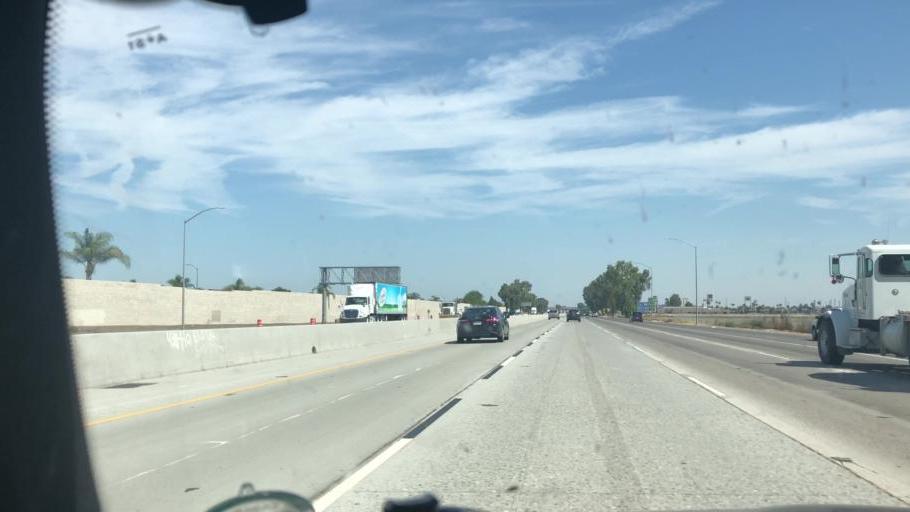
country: US
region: California
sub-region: Kern County
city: Greenfield
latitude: 35.2853
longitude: -119.0277
